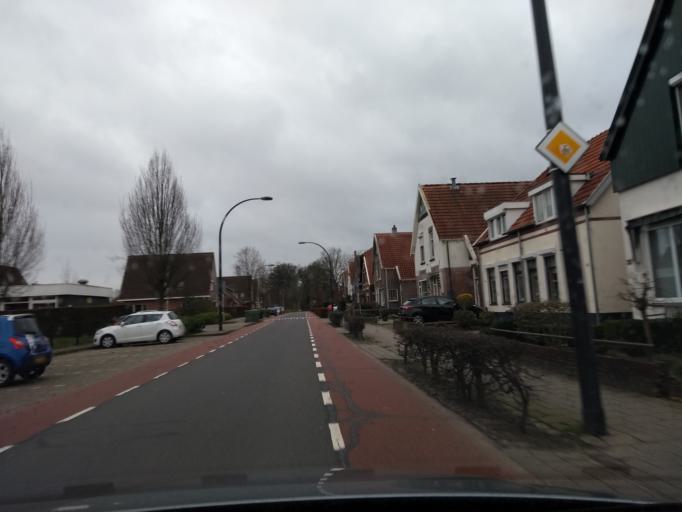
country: NL
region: Overijssel
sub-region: Gemeente Borne
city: Borne
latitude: 52.2946
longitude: 6.7461
